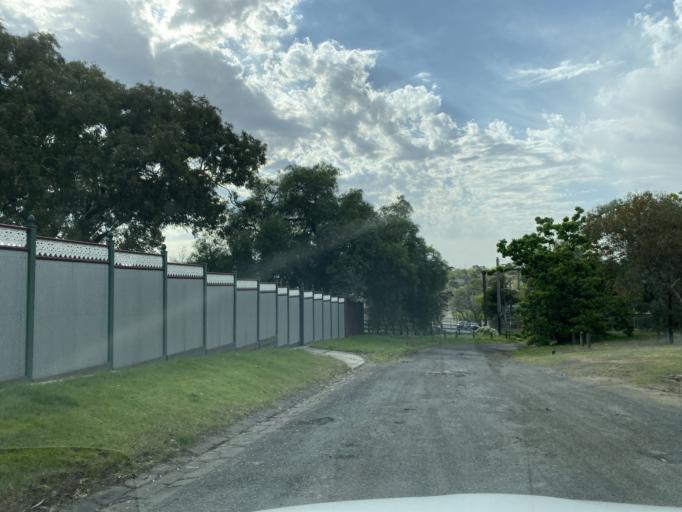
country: AU
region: Victoria
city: Balwyn
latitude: -37.8275
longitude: 145.0693
